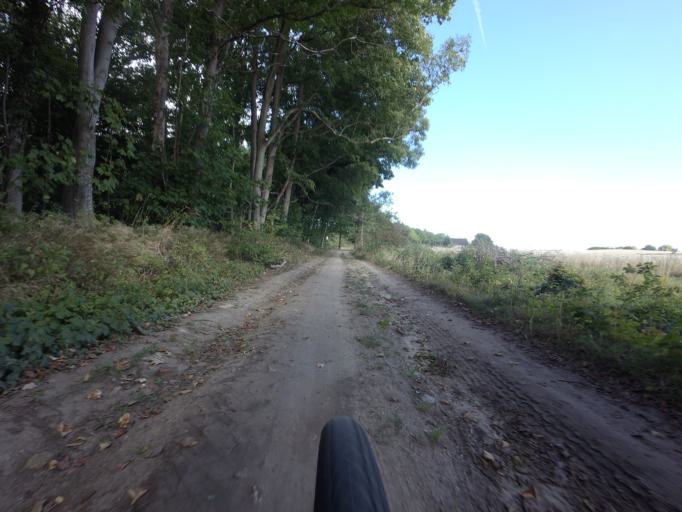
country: DK
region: Zealand
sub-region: Vordingborg Kommune
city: Stege
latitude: 54.9697
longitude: 12.4146
